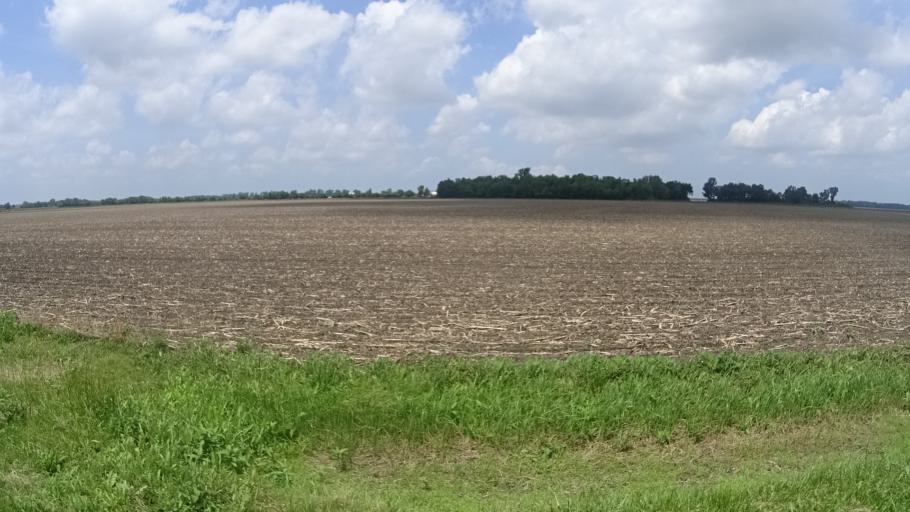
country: US
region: Ohio
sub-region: Huron County
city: Bellevue
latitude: 41.2983
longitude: -82.7738
